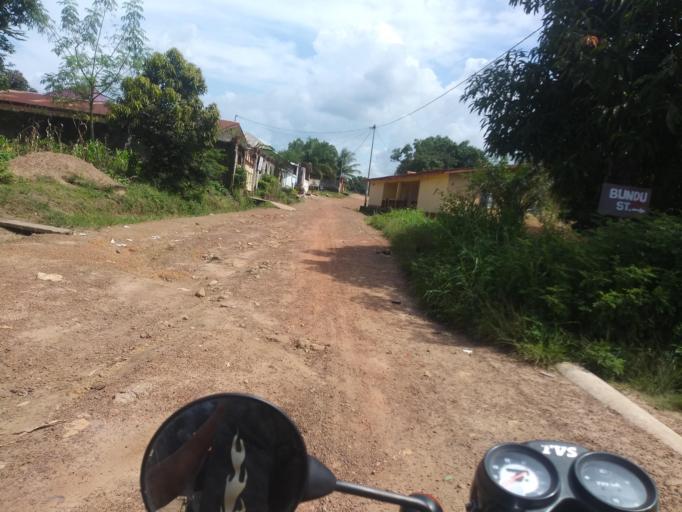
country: SL
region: Northern Province
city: Makeni
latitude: 8.8807
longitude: -12.0354
